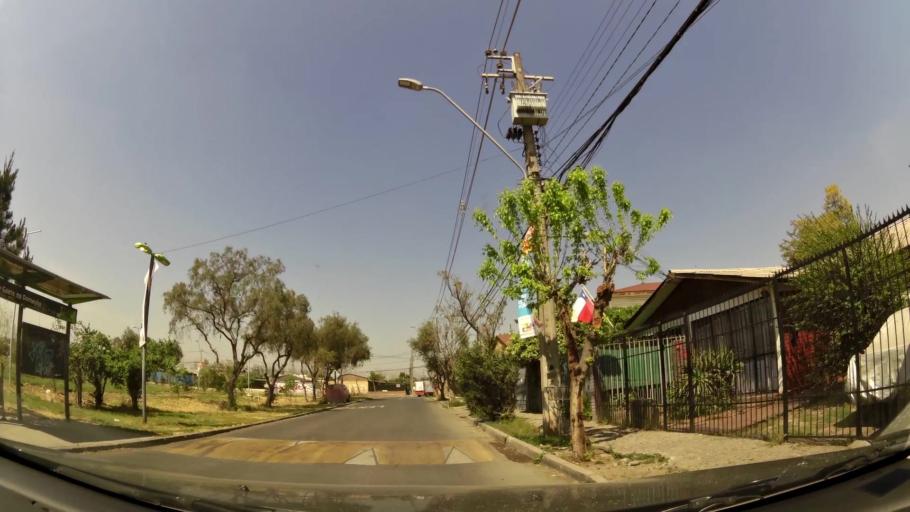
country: CL
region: Santiago Metropolitan
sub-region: Provincia de Maipo
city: San Bernardo
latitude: -33.5793
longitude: -70.7108
